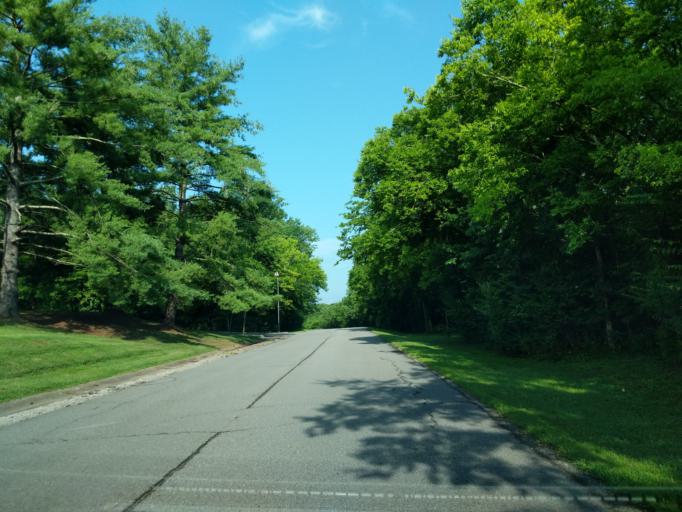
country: US
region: Tennessee
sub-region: Sumner County
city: Hendersonville
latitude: 36.3004
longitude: -86.6501
